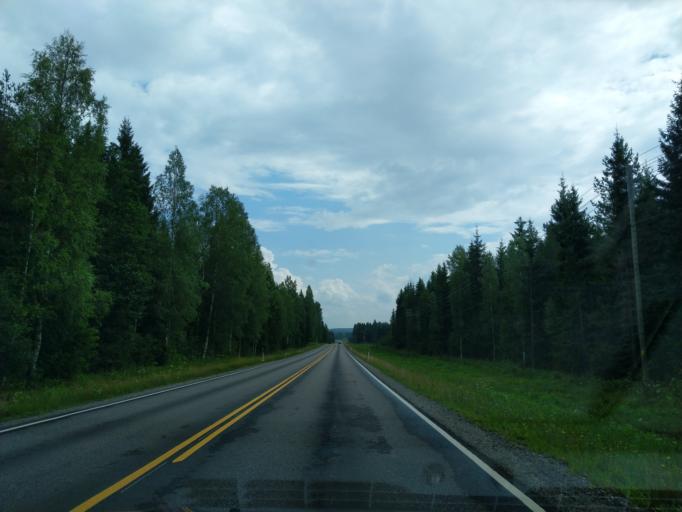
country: FI
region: South Karelia
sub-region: Imatra
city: Parikkala
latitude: 61.6147
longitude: 29.4495
